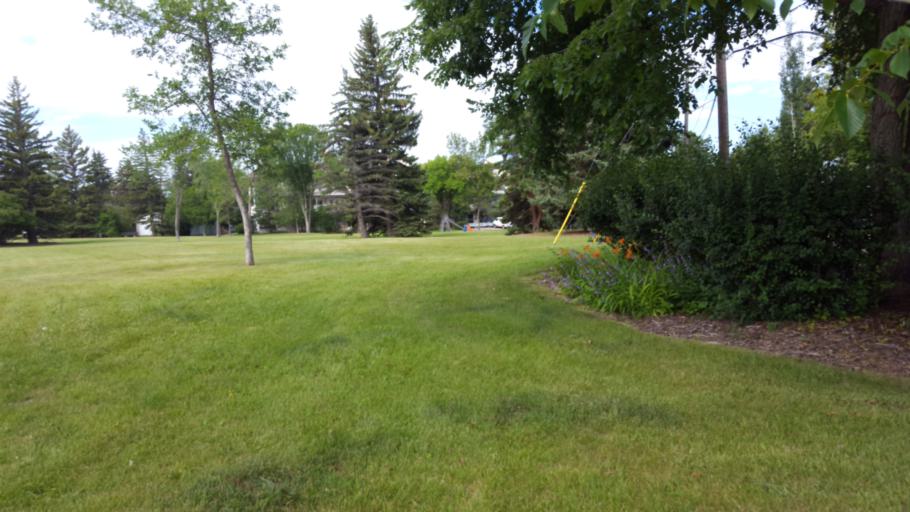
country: CA
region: Alberta
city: Edmonton
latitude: 53.5155
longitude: -113.5295
